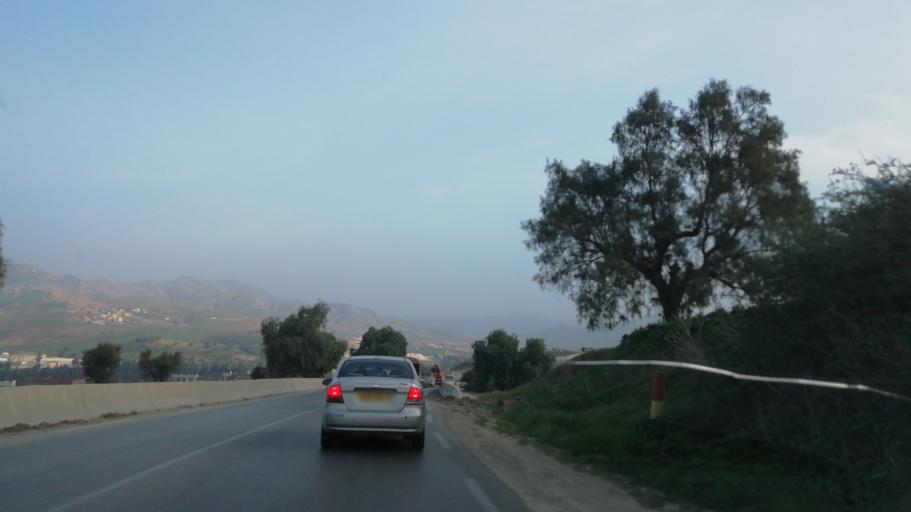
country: DZ
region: Mascara
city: Bou Hanifia el Hamamat
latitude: 35.4723
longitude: -0.0164
